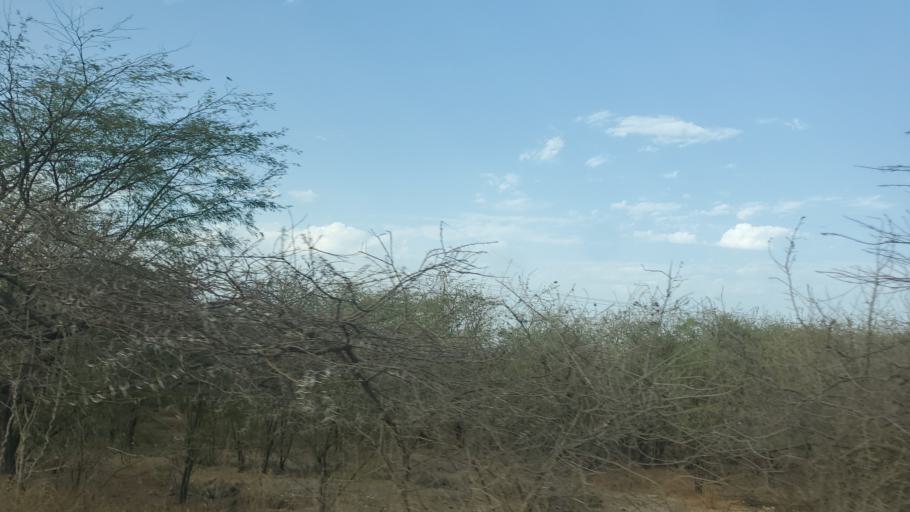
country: SN
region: Saint-Louis
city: Saint-Louis
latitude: 15.9454
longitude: -16.4330
